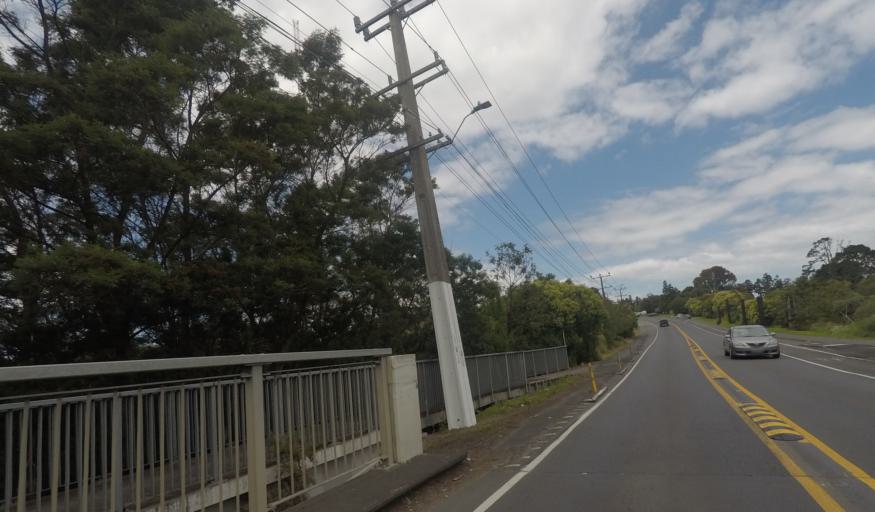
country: NZ
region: Auckland
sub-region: Auckland
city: Rosebank
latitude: -36.8483
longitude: 174.6277
